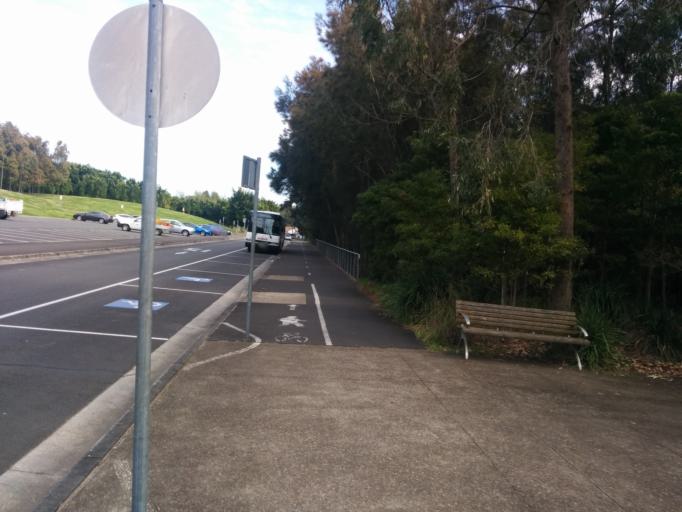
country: AU
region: New South Wales
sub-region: Canada Bay
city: Concord West
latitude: -33.8467
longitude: 151.0774
